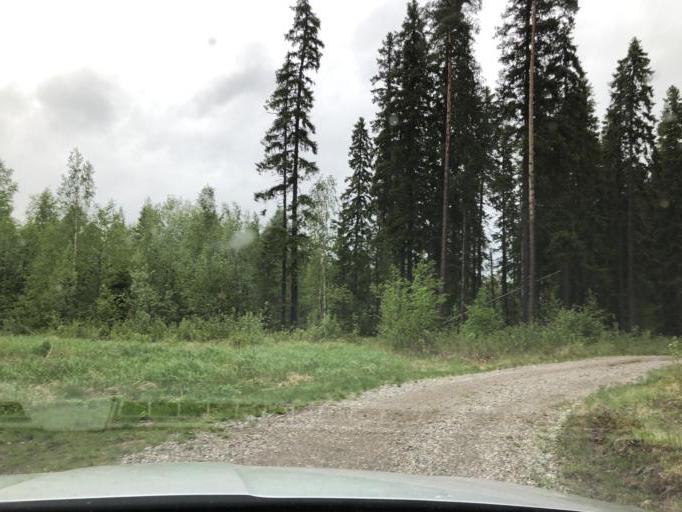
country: SE
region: Norrbotten
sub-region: Pitea Kommun
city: Roknas
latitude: 65.3998
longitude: 21.2633
